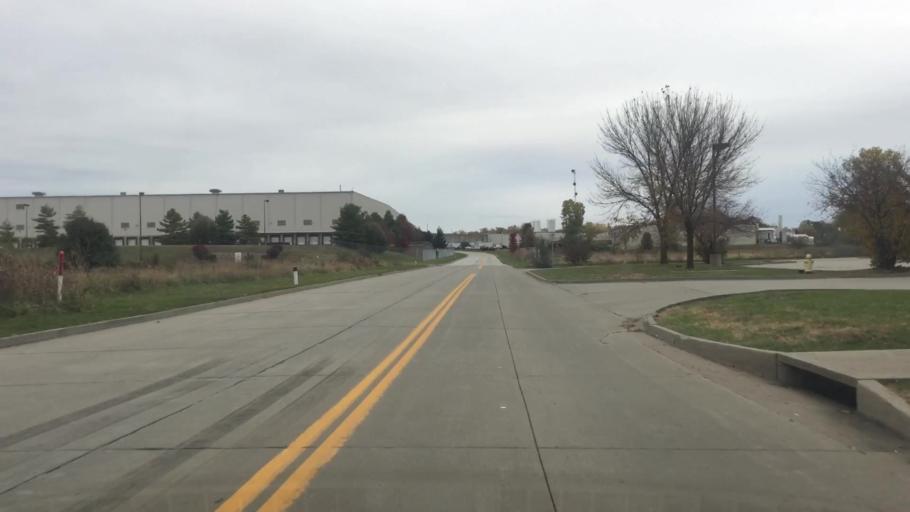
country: US
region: Missouri
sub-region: Jackson County
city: Lees Summit
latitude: 38.8814
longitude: -94.3629
